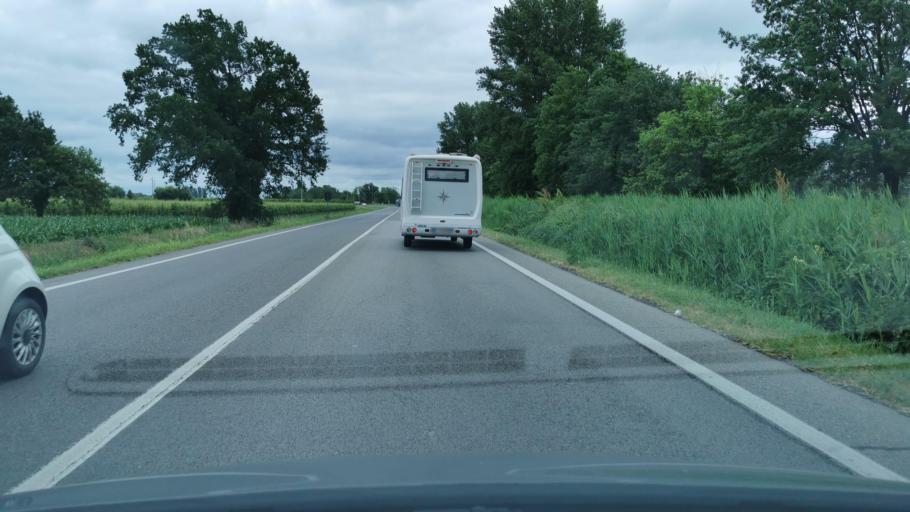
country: IT
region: Emilia-Romagna
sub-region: Provincia di Ravenna
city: Granarolo
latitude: 44.3469
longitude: 11.9247
